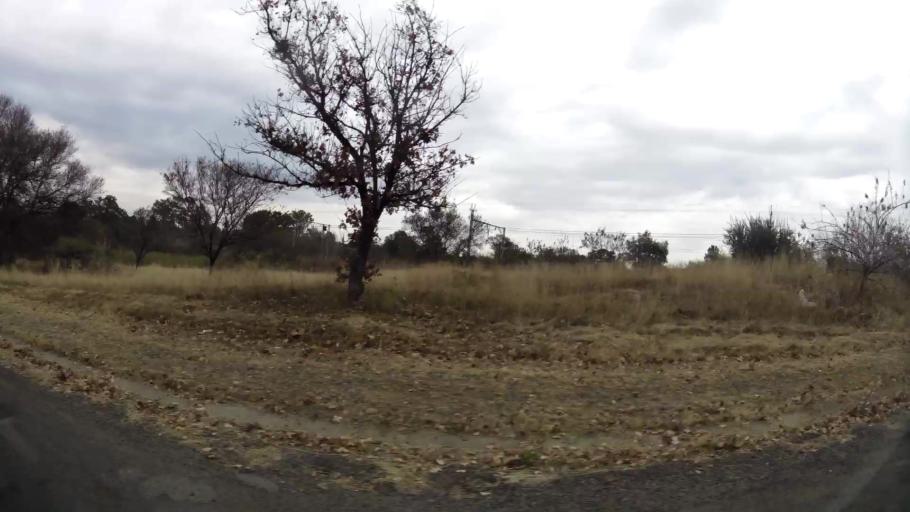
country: ZA
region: Orange Free State
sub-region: Fezile Dabi District Municipality
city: Kroonstad
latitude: -27.6488
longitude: 27.2444
